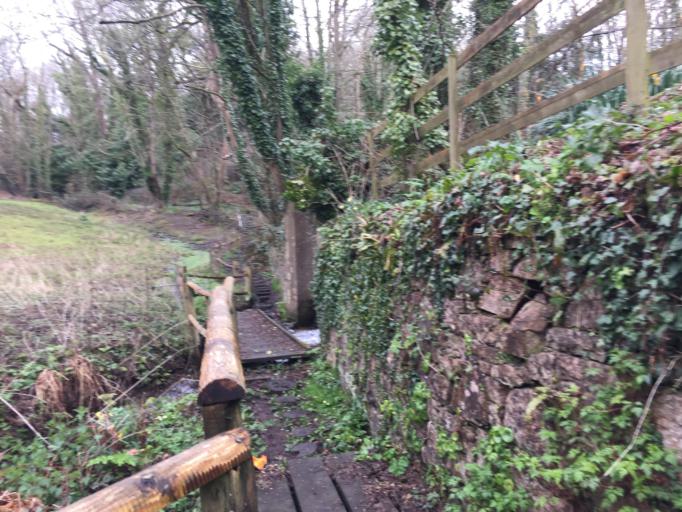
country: JE
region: St Helier
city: Saint Helier
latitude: 49.2149
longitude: -2.1340
